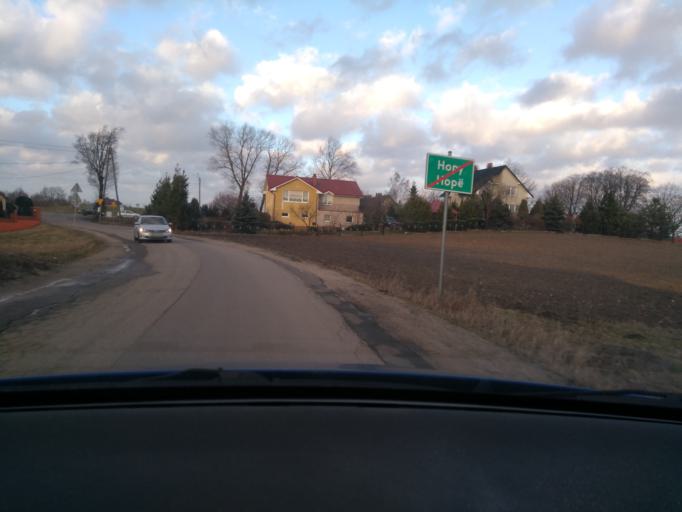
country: PL
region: Pomeranian Voivodeship
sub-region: Powiat kartuski
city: Przodkowo
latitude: 54.3996
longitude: 18.2231
